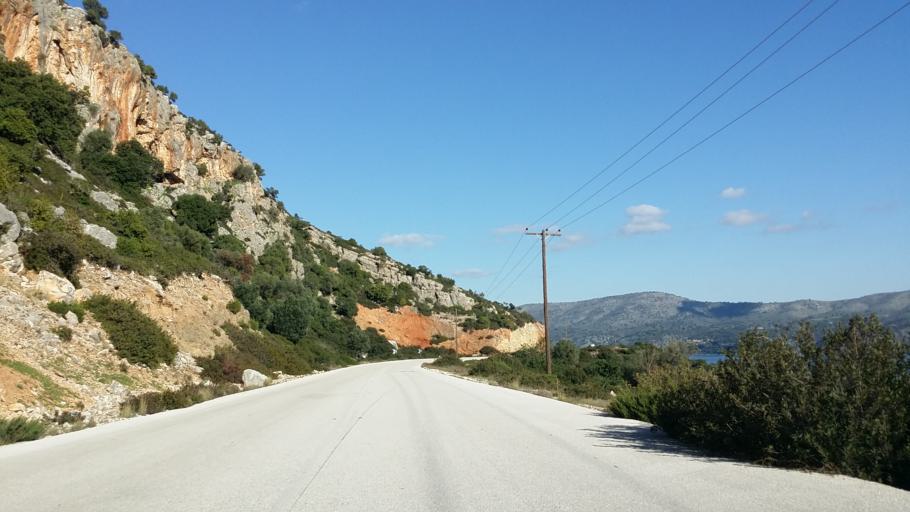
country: GR
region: West Greece
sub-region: Nomos Aitolias kai Akarnanias
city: Astakos
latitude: 38.5139
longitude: 21.0511
